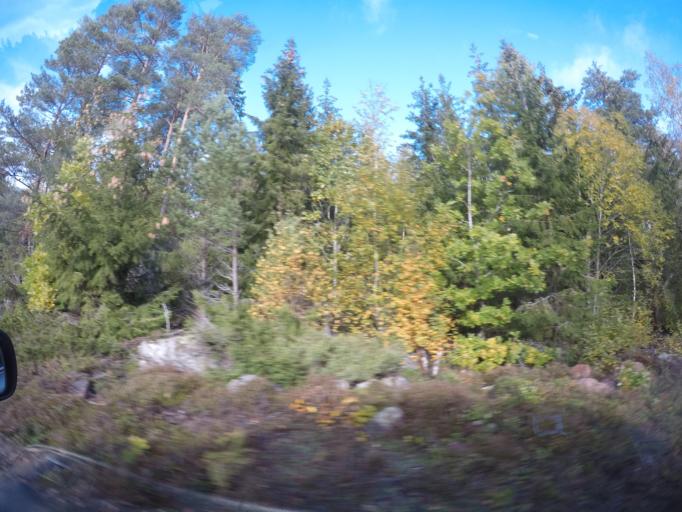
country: SE
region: Soedermanland
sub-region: Eskilstuna Kommun
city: Kvicksund
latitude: 59.3926
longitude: 16.2350
